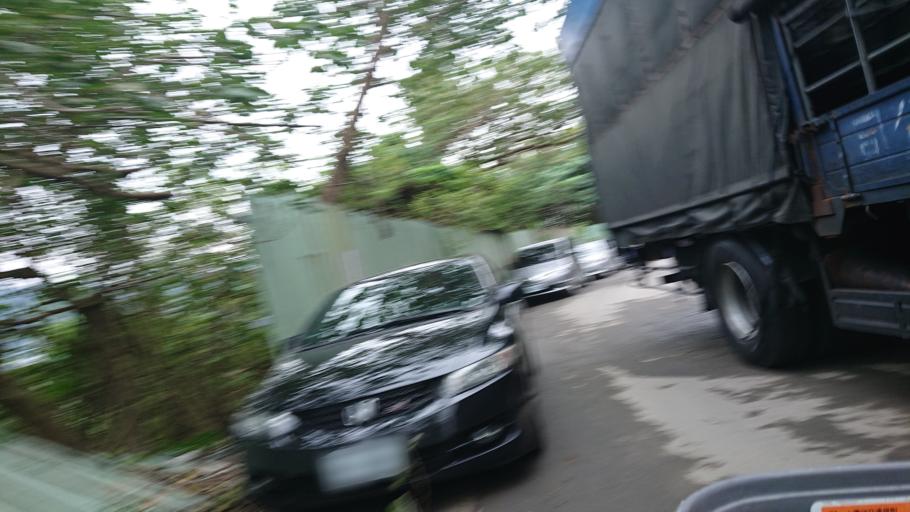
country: TW
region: Taiwan
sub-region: Taoyuan
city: Taoyuan
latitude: 24.9437
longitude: 121.3955
